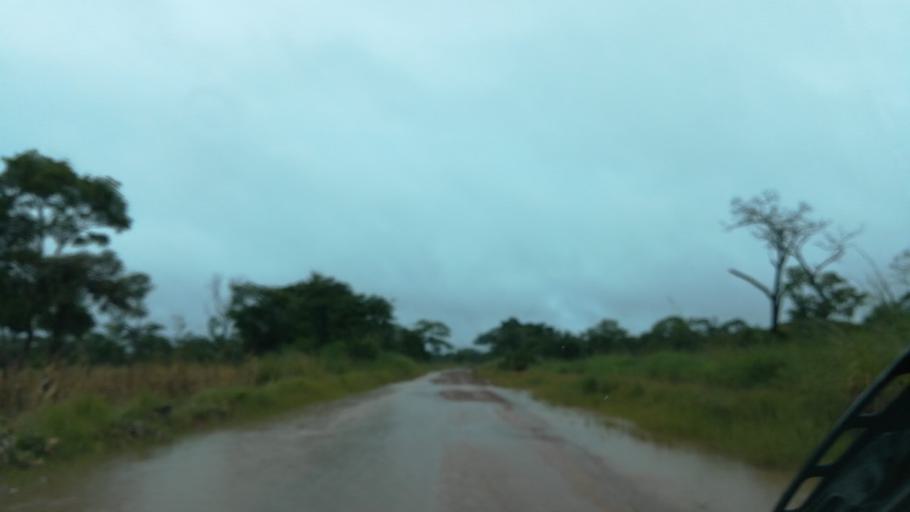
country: ZM
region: Luapula
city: Mwense
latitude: -10.7162
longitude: 28.1938
